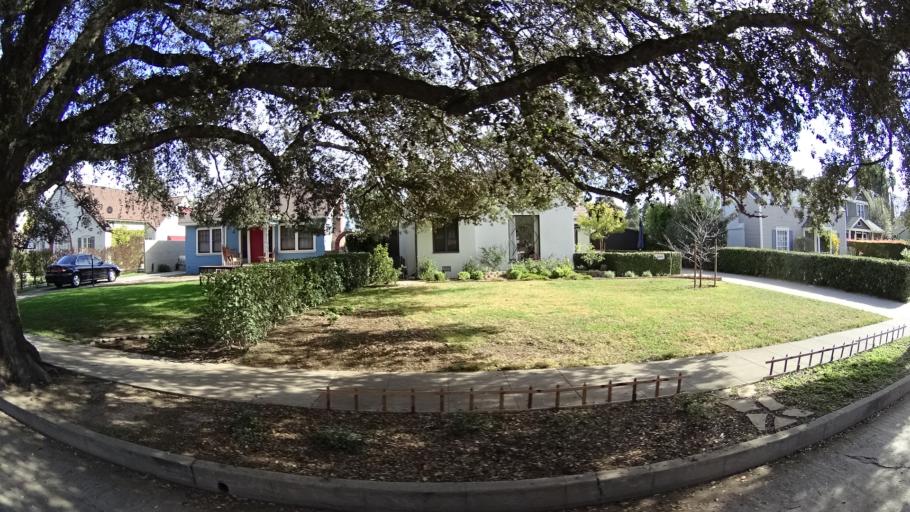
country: US
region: California
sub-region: Orange County
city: Santa Ana
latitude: 33.7642
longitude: -117.8738
